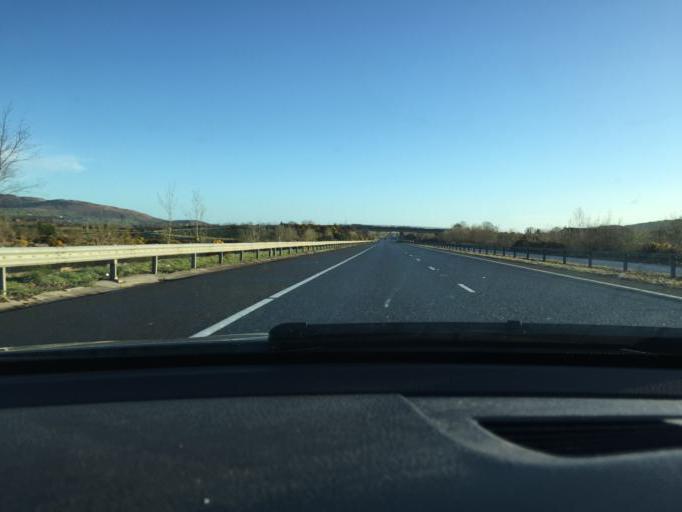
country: GB
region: Northern Ireland
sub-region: Newry and Mourne District
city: Newry
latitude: 54.1170
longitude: -6.3637
